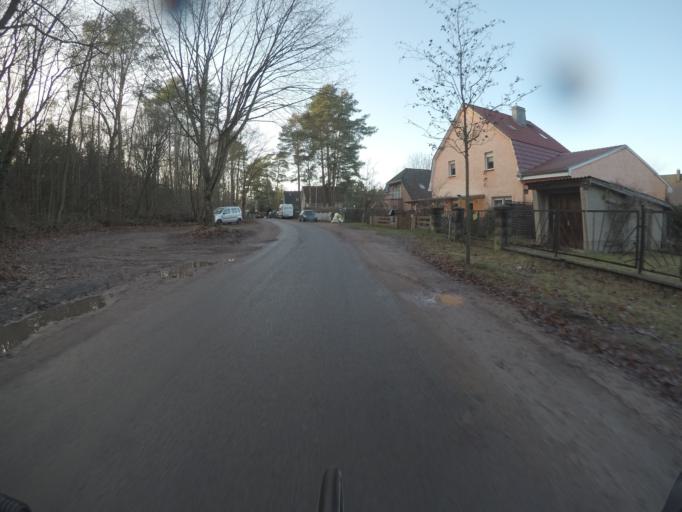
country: DE
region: Brandenburg
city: Birkenwerder
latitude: 52.6852
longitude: 13.3166
